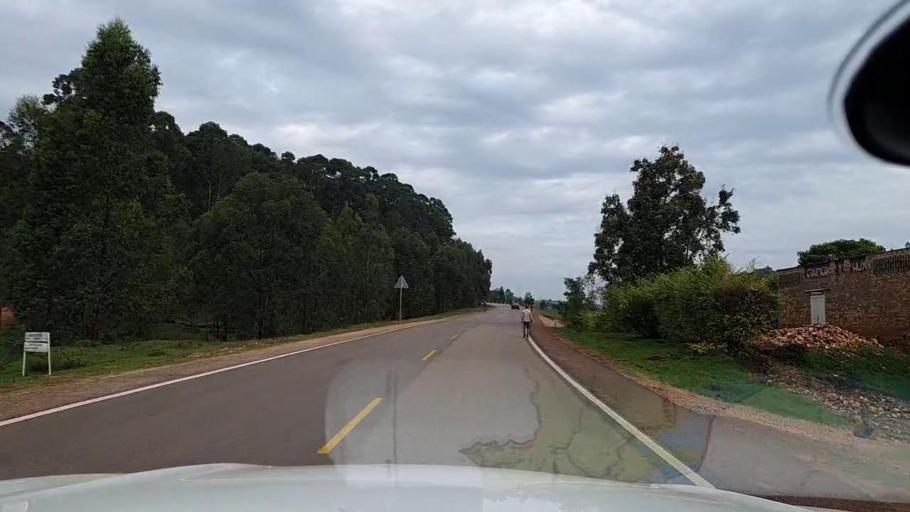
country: RW
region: Southern Province
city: Butare
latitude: -2.5644
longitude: 29.7237
